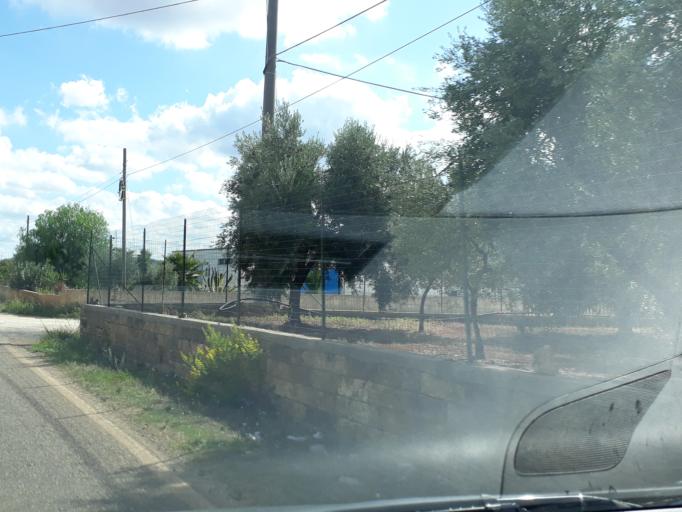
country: IT
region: Apulia
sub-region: Provincia di Brindisi
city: Pezze di Greco
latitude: 40.8021
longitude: 17.3983
